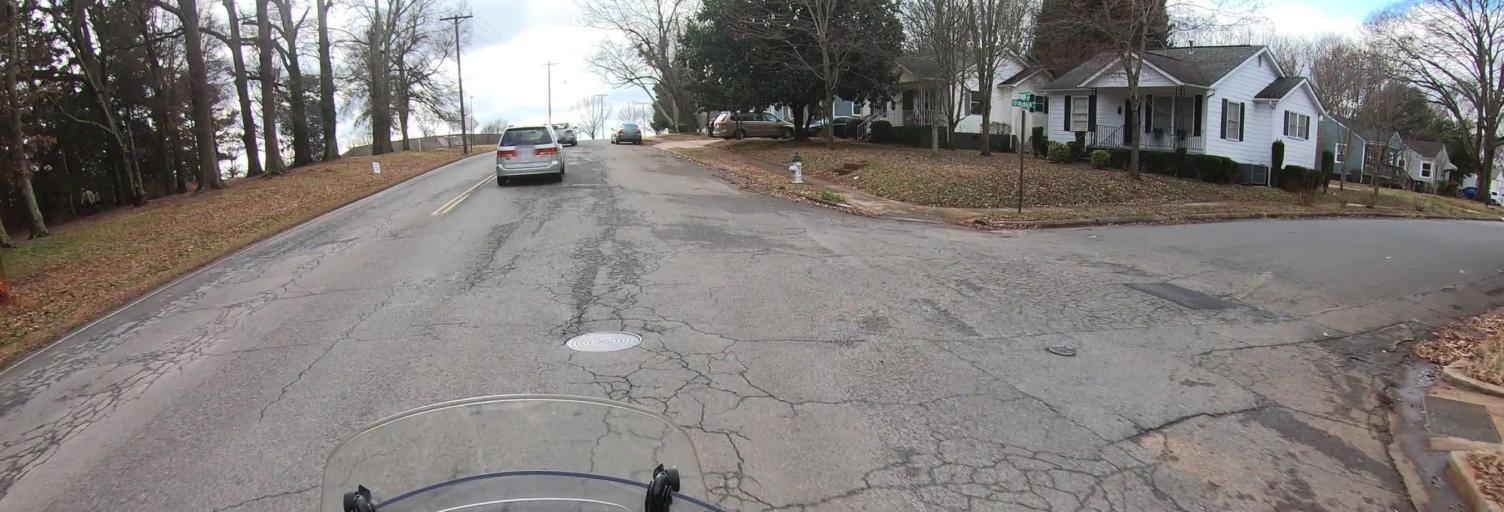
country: US
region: South Carolina
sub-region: York County
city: Rock Hill
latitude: 34.9505
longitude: -81.0111
